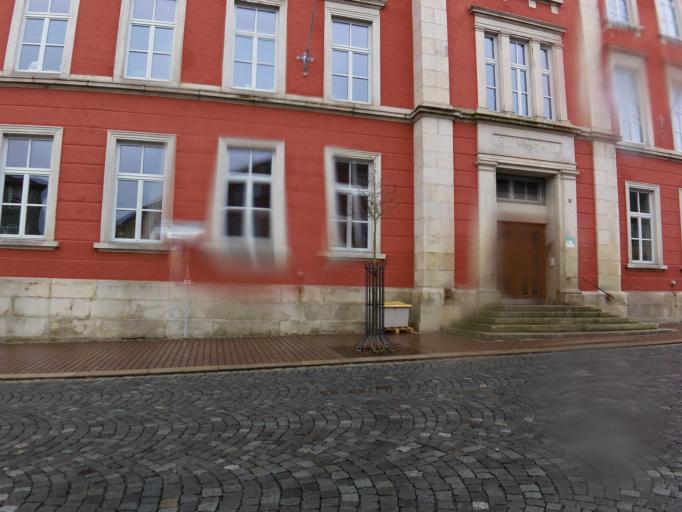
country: DE
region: Bavaria
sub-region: Upper Franconia
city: Wunsiedel
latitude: 50.0358
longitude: 12.0030
